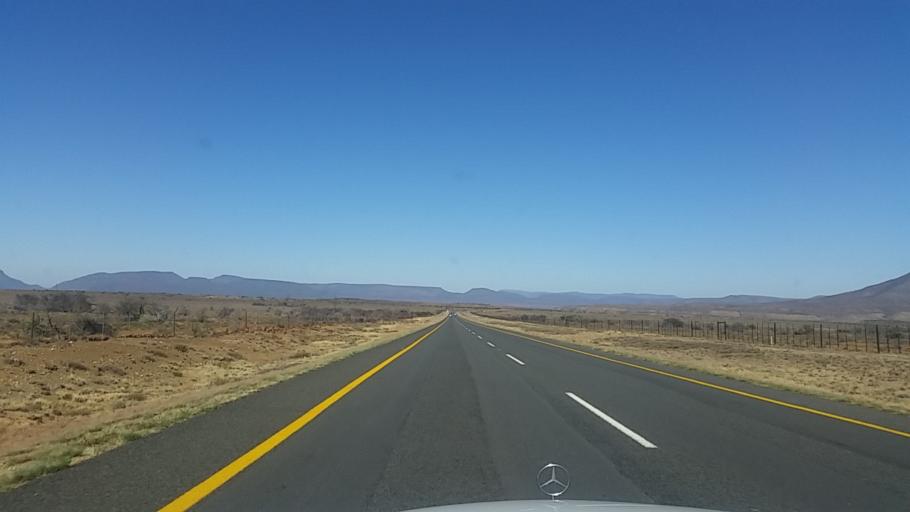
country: ZA
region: Eastern Cape
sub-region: Cacadu District Municipality
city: Graaff-Reinet
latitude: -32.1243
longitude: 24.5981
